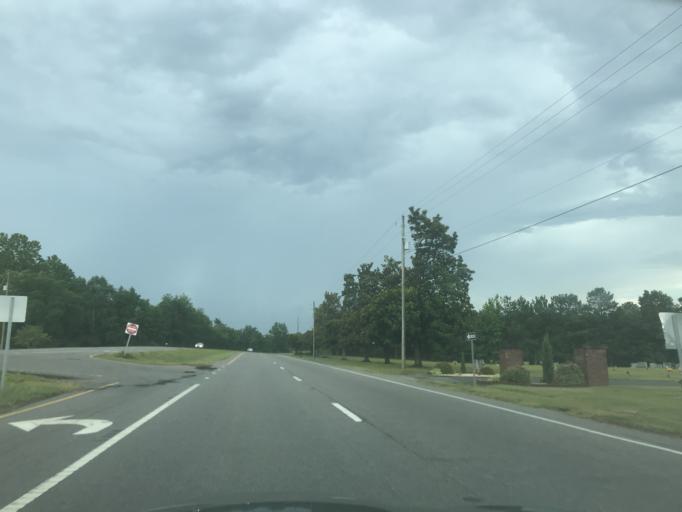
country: US
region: North Carolina
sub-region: Johnston County
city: Wilsons Mills
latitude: 35.5723
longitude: -78.3955
